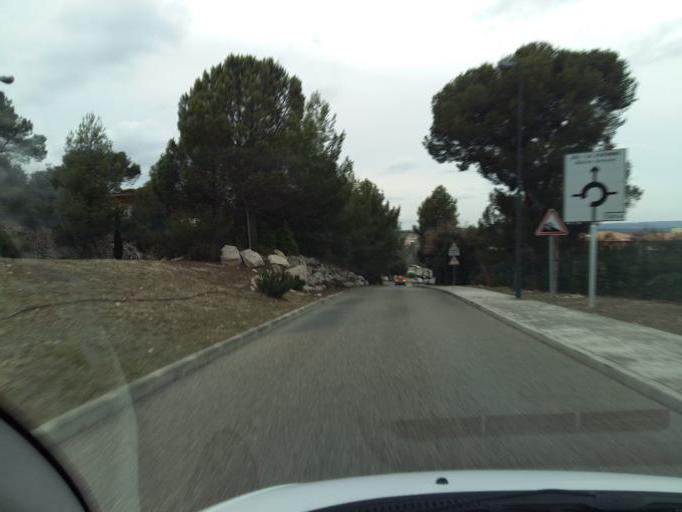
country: FR
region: Provence-Alpes-Cote d'Azur
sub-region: Departement des Bouches-du-Rhone
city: Cabries
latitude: 43.4891
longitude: 5.3582
